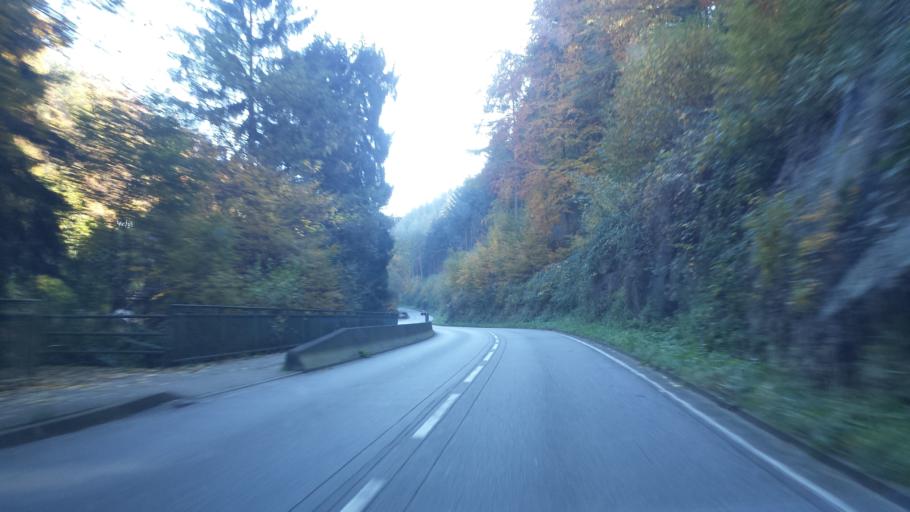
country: DE
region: Hesse
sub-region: Regierungsbezirk Darmstadt
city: Seeheim-Jugenheim
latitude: 49.7482
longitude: 8.6468
